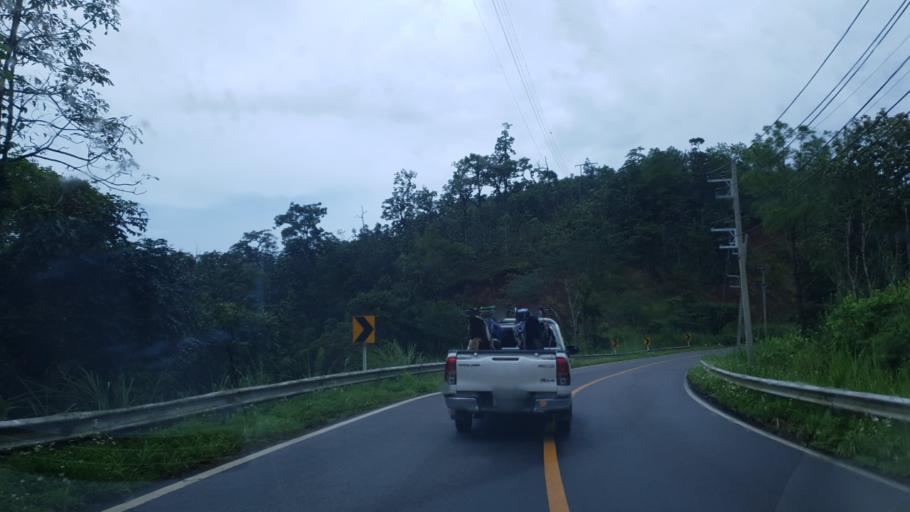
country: TH
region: Mae Hong Son
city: Ban Huai I Huak
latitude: 18.1569
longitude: 98.0284
